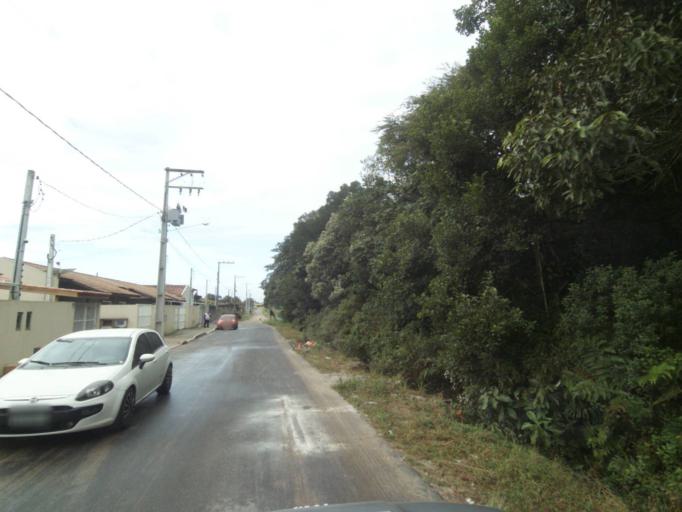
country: BR
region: Parana
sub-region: Paranagua
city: Paranagua
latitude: -25.5667
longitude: -48.5759
